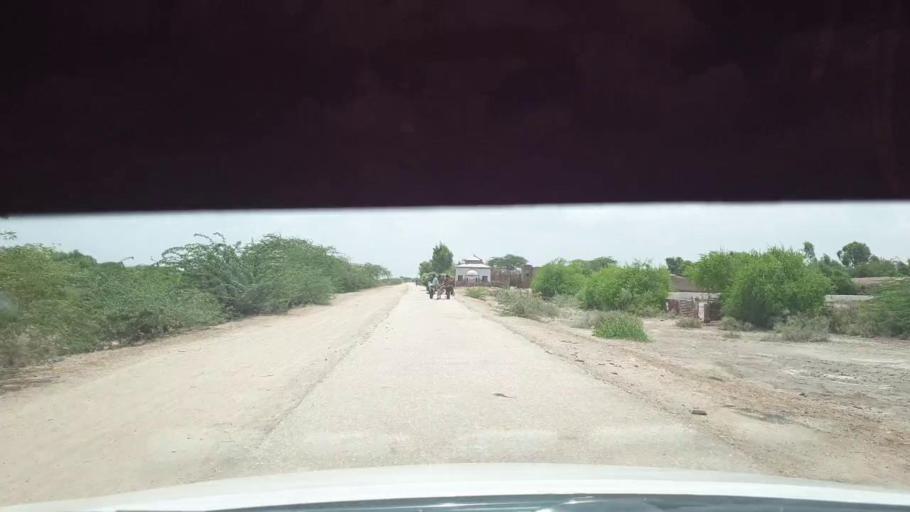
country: PK
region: Sindh
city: Kadhan
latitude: 24.4818
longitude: 68.9927
